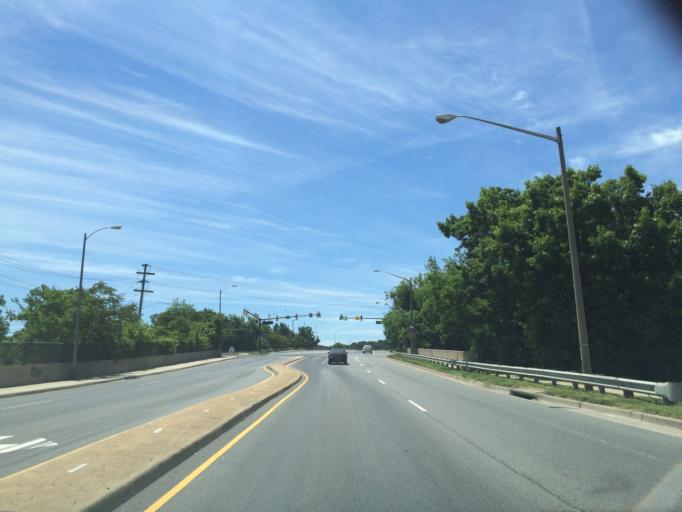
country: US
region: Virginia
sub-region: Fairfax County
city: Lincolnia
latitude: 38.8038
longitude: -77.1340
